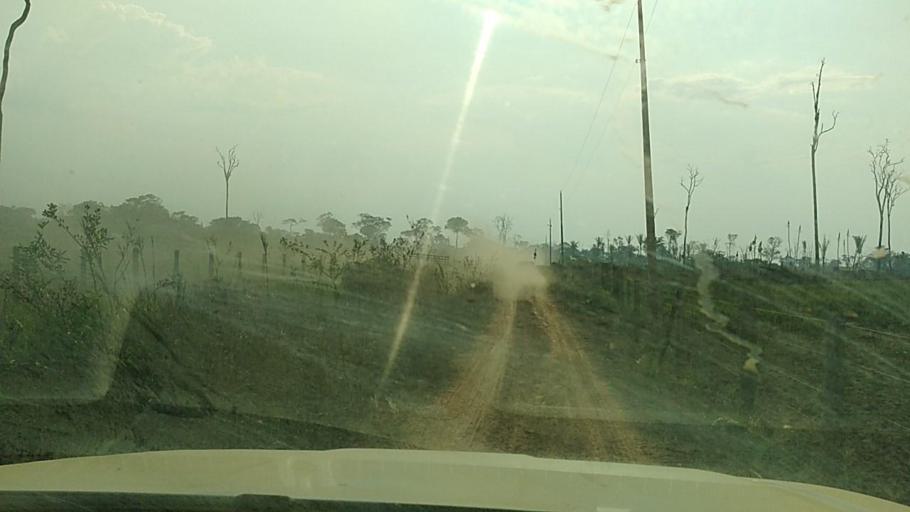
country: BR
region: Rondonia
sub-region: Porto Velho
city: Porto Velho
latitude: -8.5629
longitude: -64.0450
